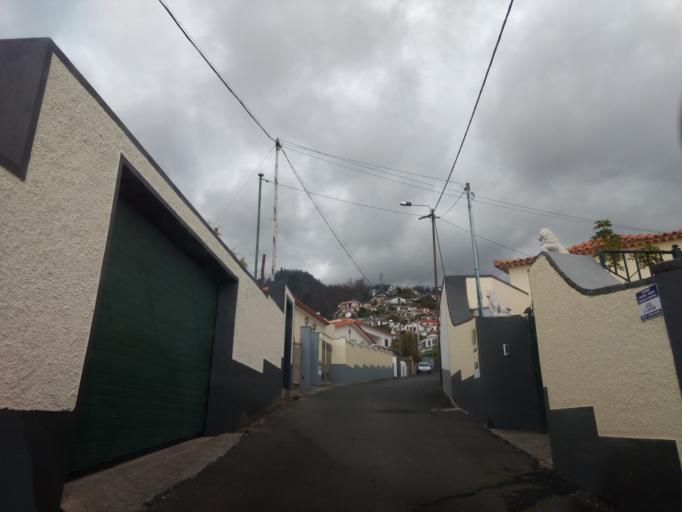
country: PT
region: Madeira
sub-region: Funchal
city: Nossa Senhora do Monte
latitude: 32.6697
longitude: -16.9350
